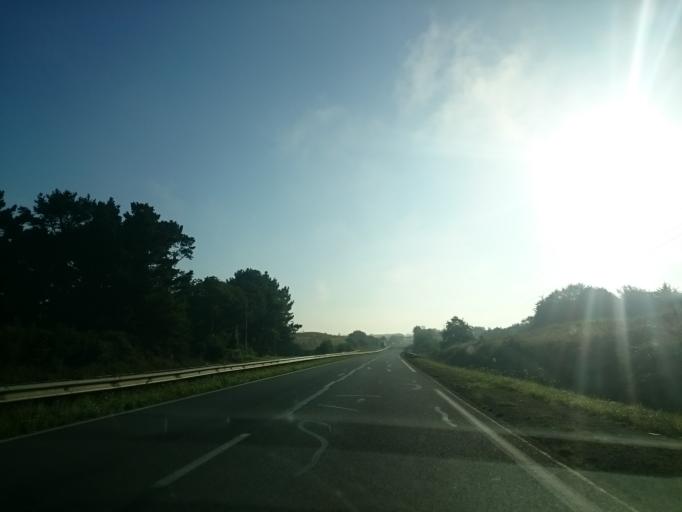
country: FR
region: Brittany
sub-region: Departement du Finistere
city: Guipavas
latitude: 48.4463
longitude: -4.3950
